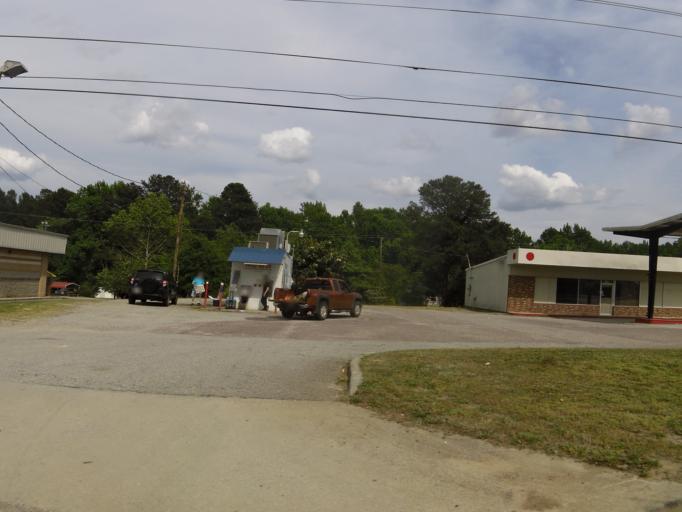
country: US
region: Georgia
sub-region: McDuffie County
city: Thomson
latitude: 33.4955
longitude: -82.5040
